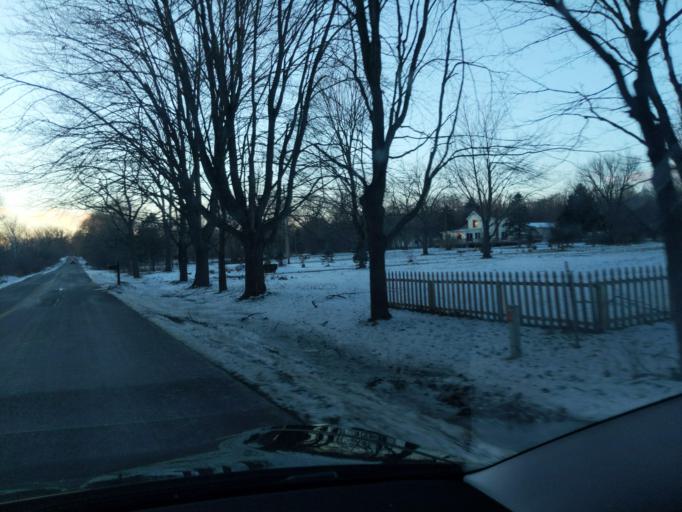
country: US
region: Michigan
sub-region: Ingham County
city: Leslie
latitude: 42.4754
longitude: -84.3088
